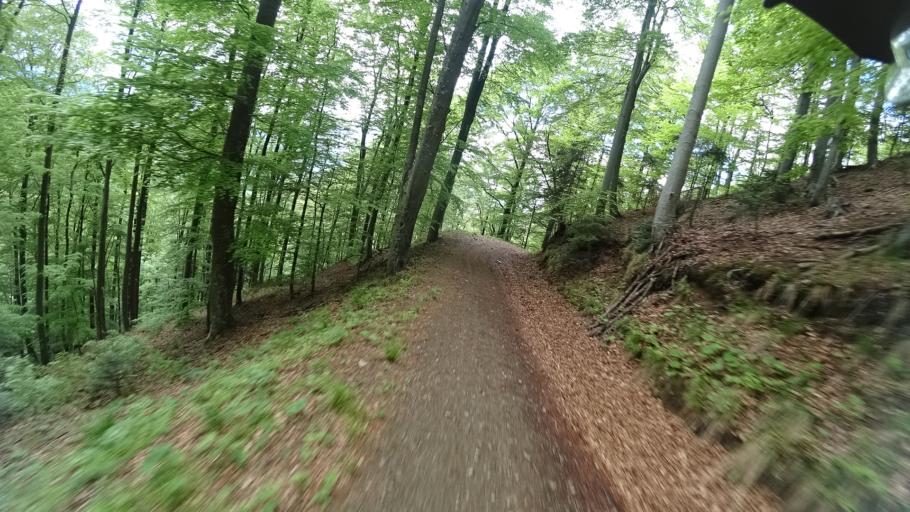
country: HR
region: Grad Zagreb
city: Kasina
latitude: 45.8906
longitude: 15.9300
